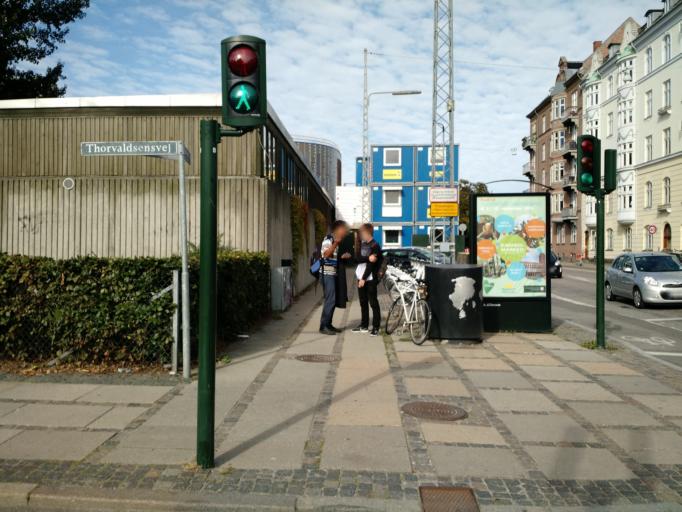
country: DK
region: Capital Region
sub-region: Frederiksberg Kommune
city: Frederiksberg
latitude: 55.6813
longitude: 12.5439
